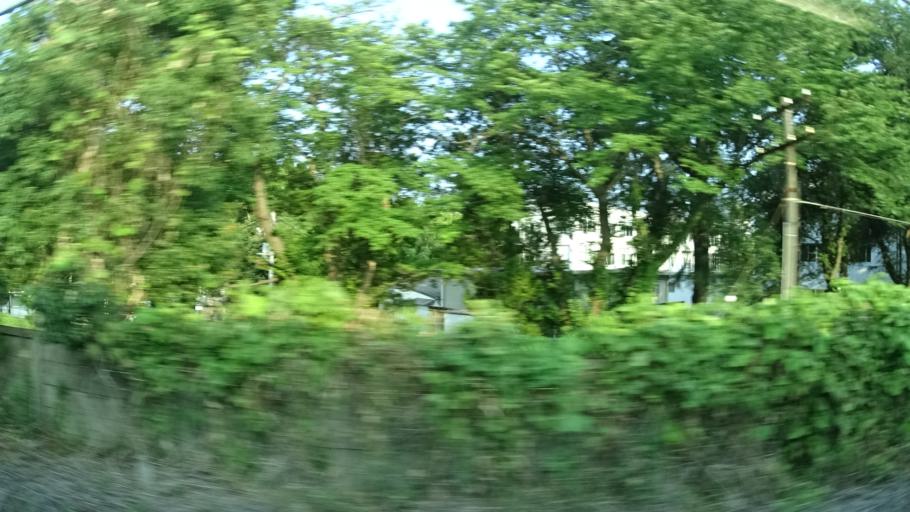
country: JP
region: Ibaraki
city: Hitachi
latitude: 36.5564
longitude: 140.6373
